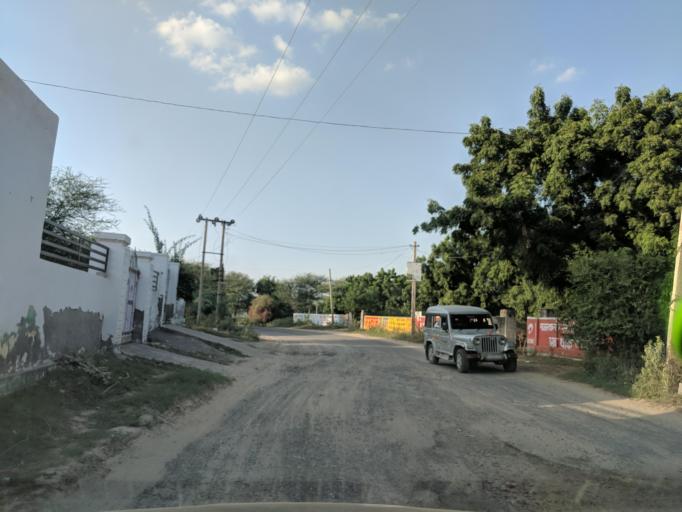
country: IN
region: Rajasthan
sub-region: Churu
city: Rajgarh
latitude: 28.5350
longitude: 75.3771
